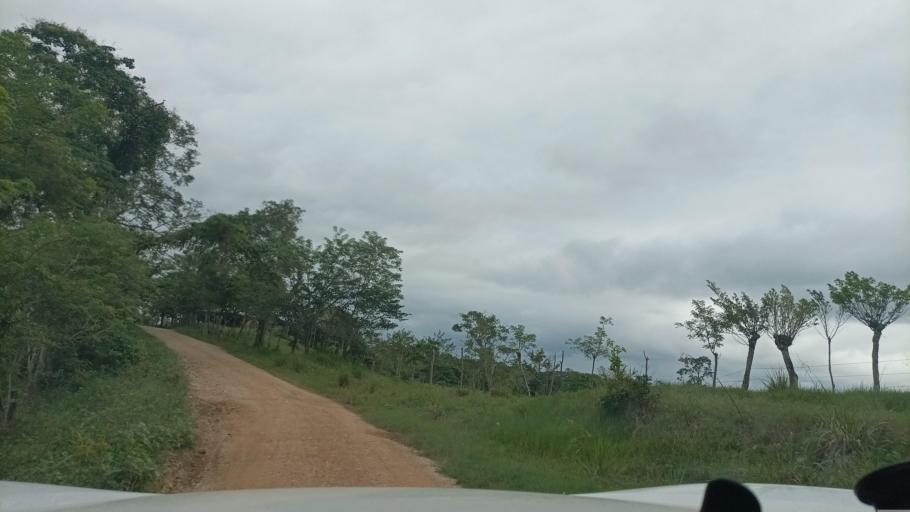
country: MX
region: Veracruz
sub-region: Uxpanapa
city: Poblado Cinco
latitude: 17.5012
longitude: -94.5640
